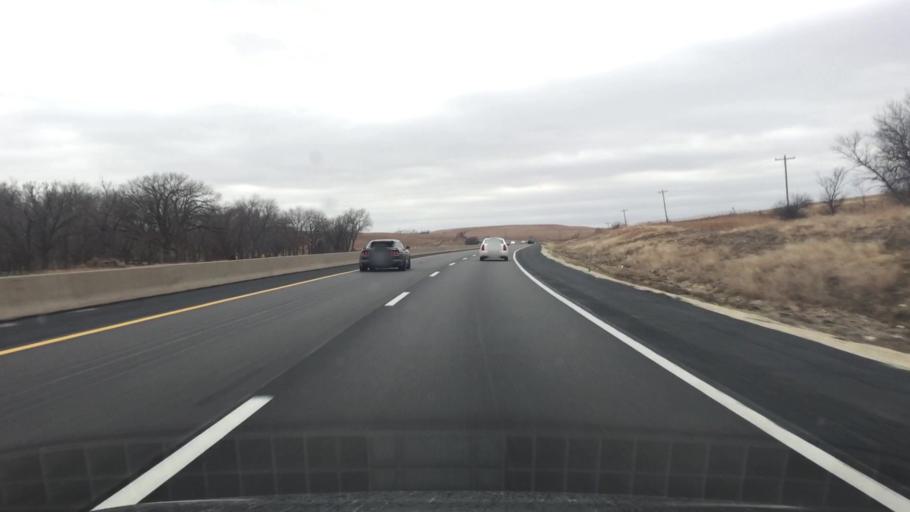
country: US
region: Kansas
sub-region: Chase County
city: Cottonwood Falls
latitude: 38.1221
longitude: -96.5572
